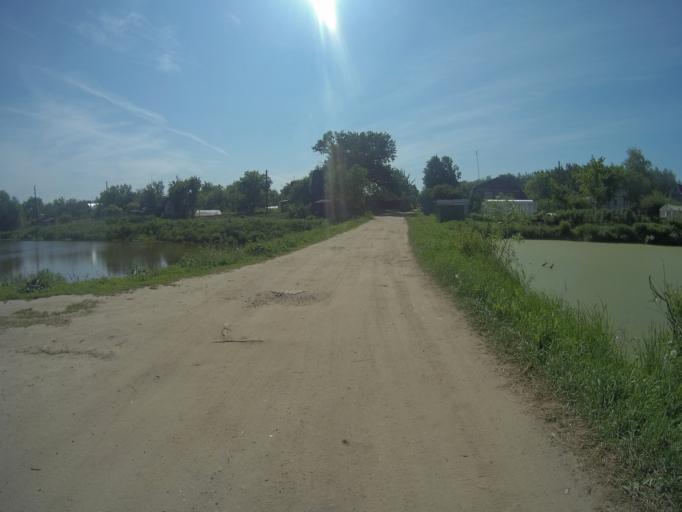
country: RU
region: Vladimir
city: Stavrovo
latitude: 56.1359
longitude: 40.0716
